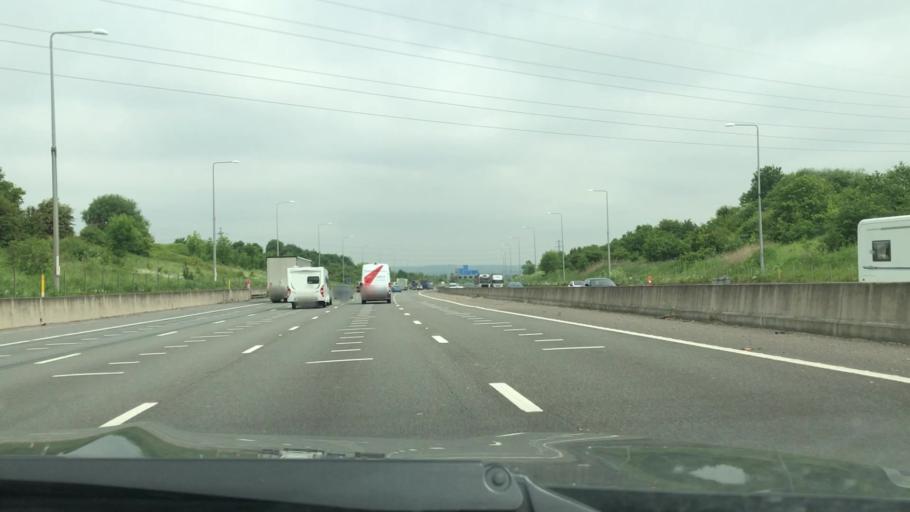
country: GB
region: England
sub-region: Greater London
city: Cranham
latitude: 51.5445
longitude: 0.2826
